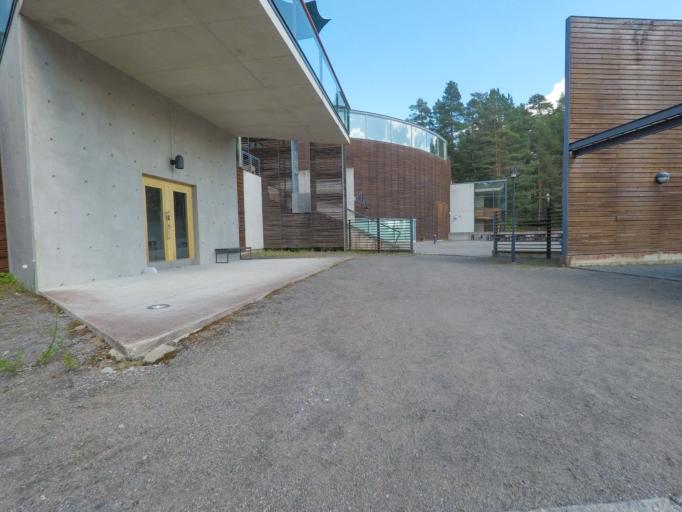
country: FI
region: Southern Savonia
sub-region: Savonlinna
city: Punkaharju
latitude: 61.7988
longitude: 29.3214
